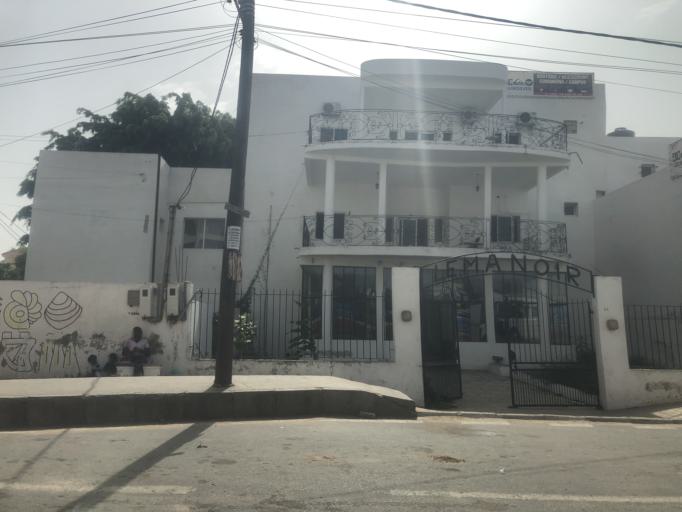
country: SN
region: Dakar
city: Mermoz Boabab
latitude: 14.7428
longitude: -17.5116
